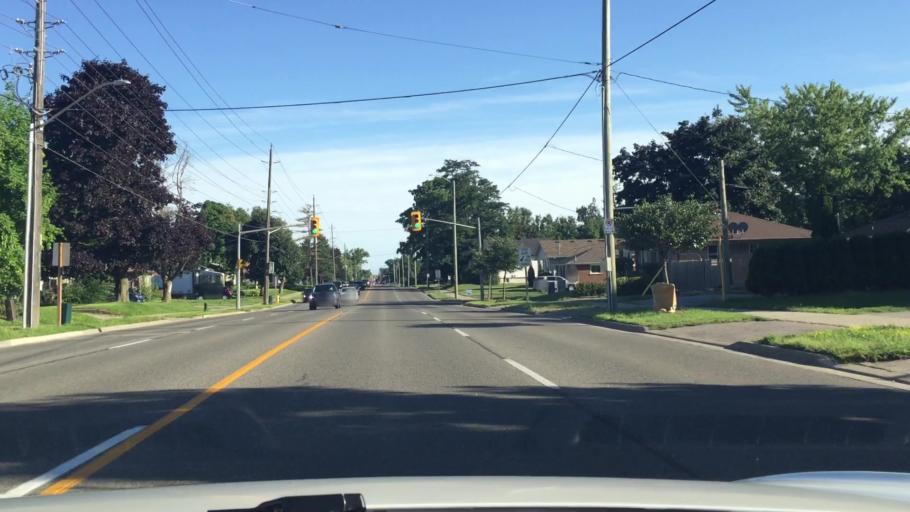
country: CA
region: Ontario
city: Oshawa
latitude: 43.9100
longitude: -78.8367
